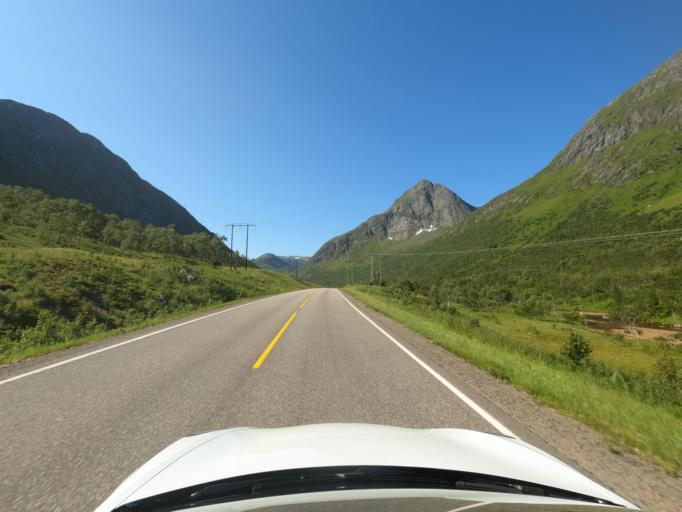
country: NO
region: Nordland
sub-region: Lodingen
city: Lodingen
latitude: 68.5091
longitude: 15.7311
